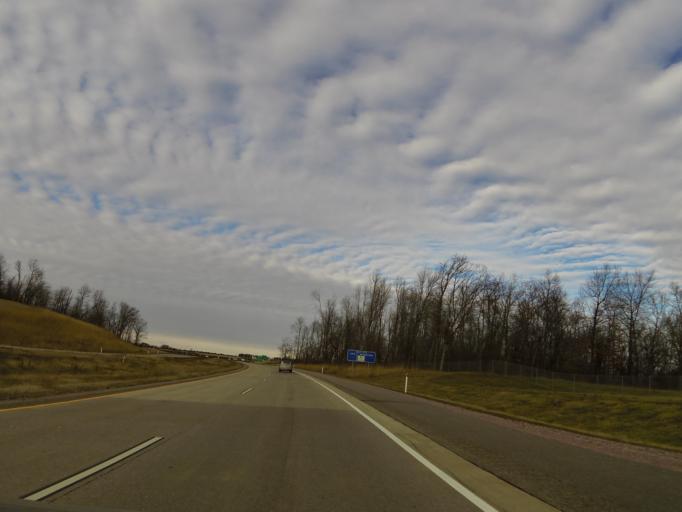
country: US
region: Wisconsin
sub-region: Sauk County
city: West Baraboo
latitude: 43.5074
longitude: -89.7814
